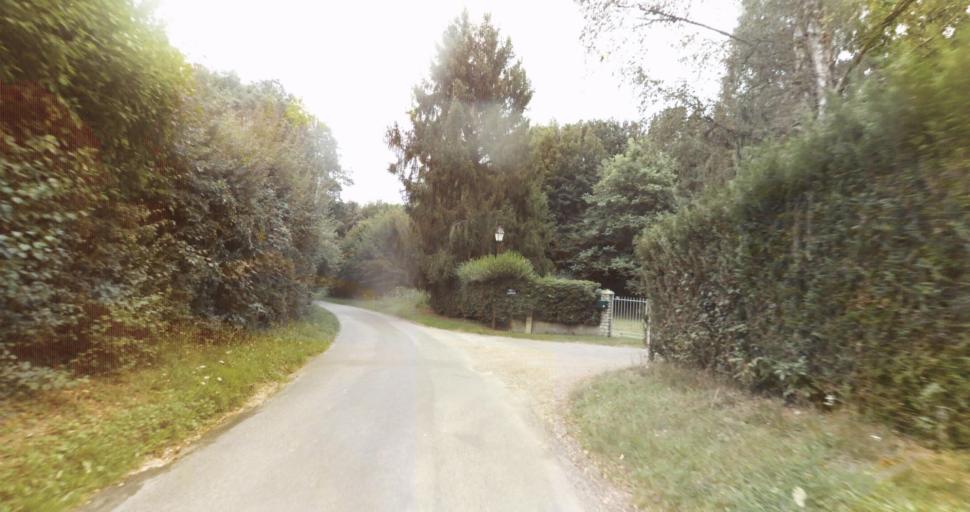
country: FR
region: Centre
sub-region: Departement d'Eure-et-Loir
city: Sorel-Moussel
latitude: 48.8602
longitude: 1.3455
